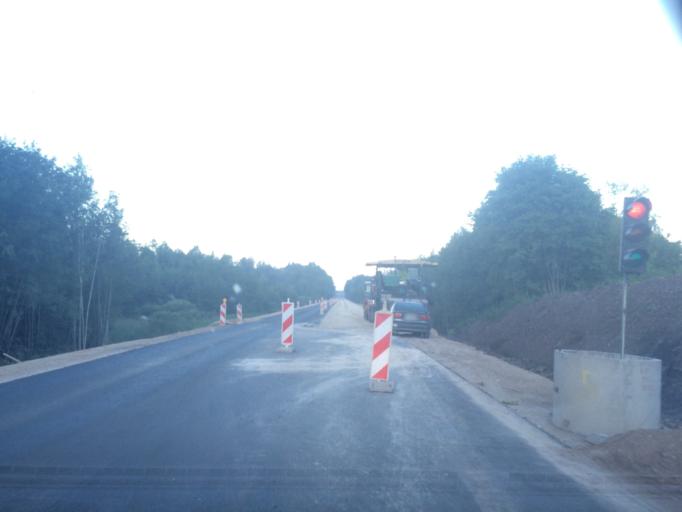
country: LT
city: Zarasai
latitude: 55.7626
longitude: 26.3345
